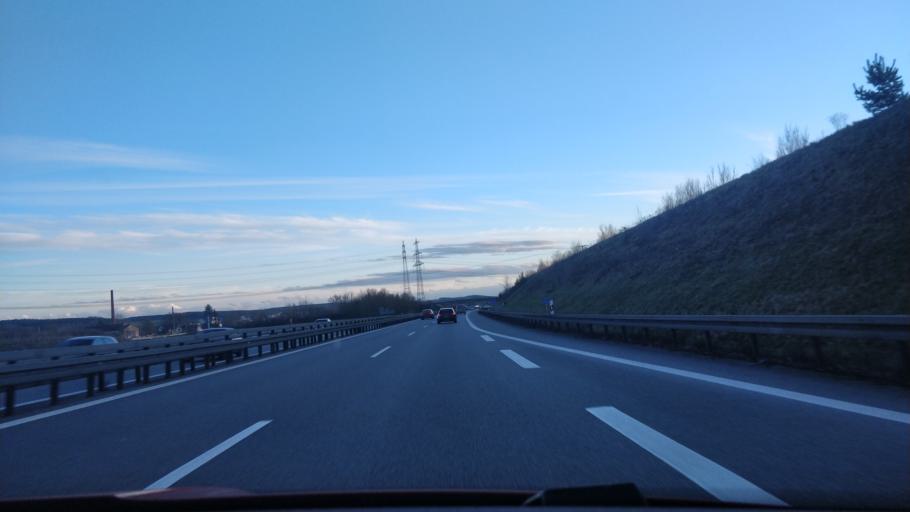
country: DE
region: Bavaria
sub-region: Upper Palatinate
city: Schirmitz
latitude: 49.6494
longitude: 12.1478
